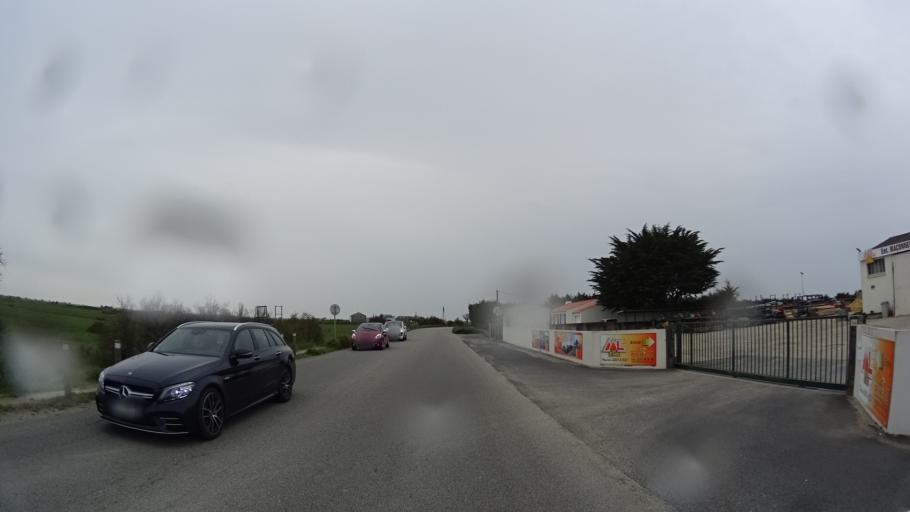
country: FR
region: Pays de la Loire
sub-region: Departement de la Vendee
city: Beauvoir-sur-Mer
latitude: 46.9063
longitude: -2.0499
